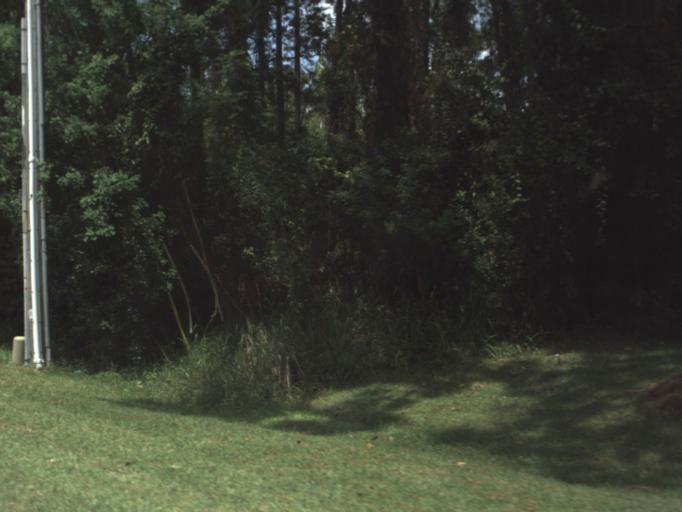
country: US
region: Florida
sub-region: Bay County
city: Hiland Park
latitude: 30.2333
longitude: -85.6108
